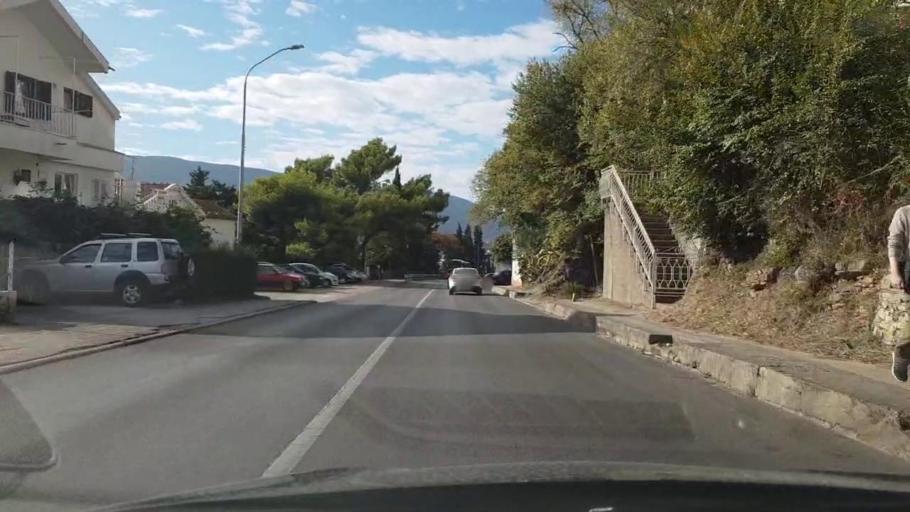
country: ME
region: Herceg Novi
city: Herceg-Novi
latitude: 42.4552
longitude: 18.5299
